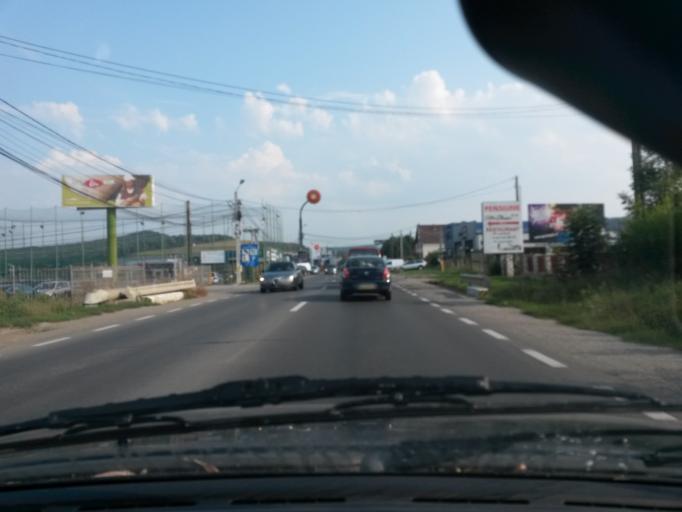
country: RO
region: Mures
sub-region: Comuna Corunca
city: Corunca
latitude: 46.5230
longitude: 24.6032
